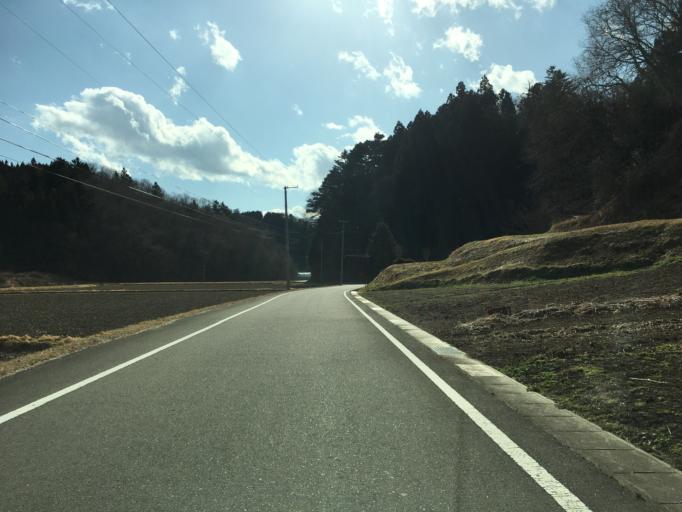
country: JP
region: Fukushima
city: Ishikawa
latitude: 37.2405
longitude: 140.5931
